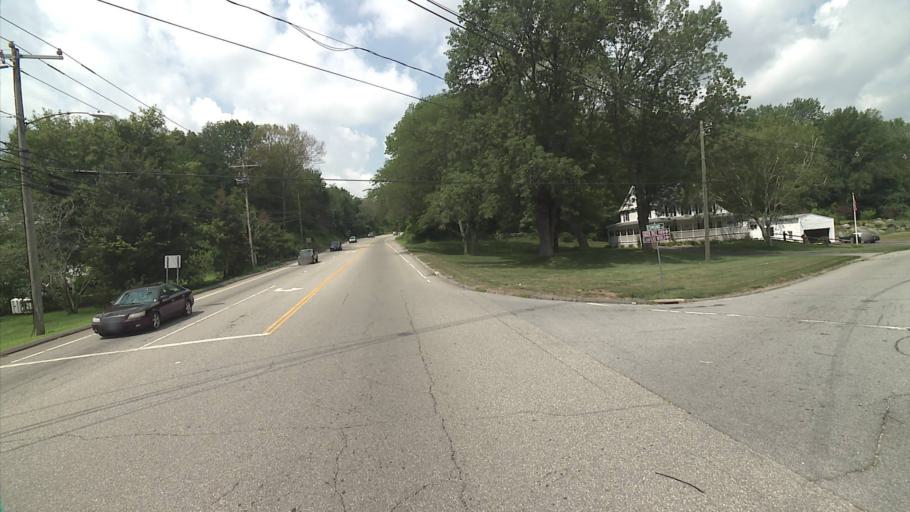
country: US
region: Connecticut
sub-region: New London County
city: Jewett City
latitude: 41.5846
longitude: -71.9411
